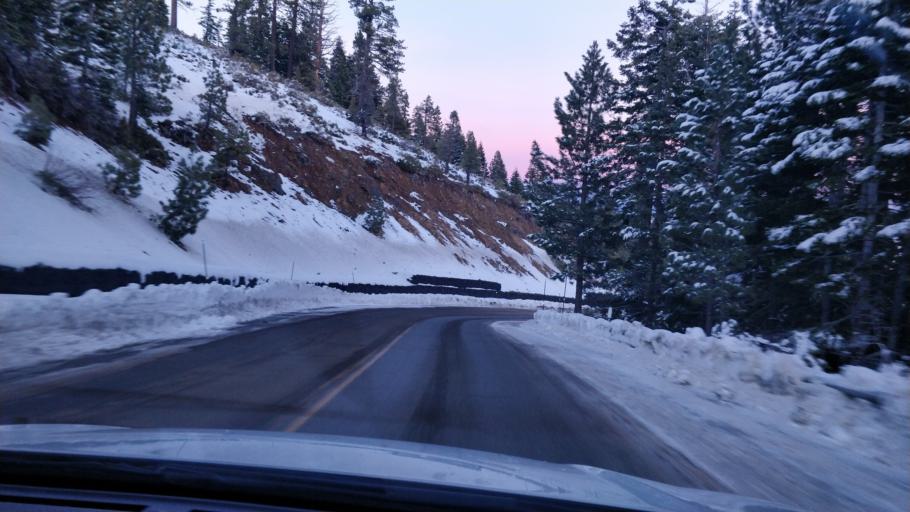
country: US
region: California
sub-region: Placer County
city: Sunnyside-Tahoe City
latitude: 39.1422
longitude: -120.1643
